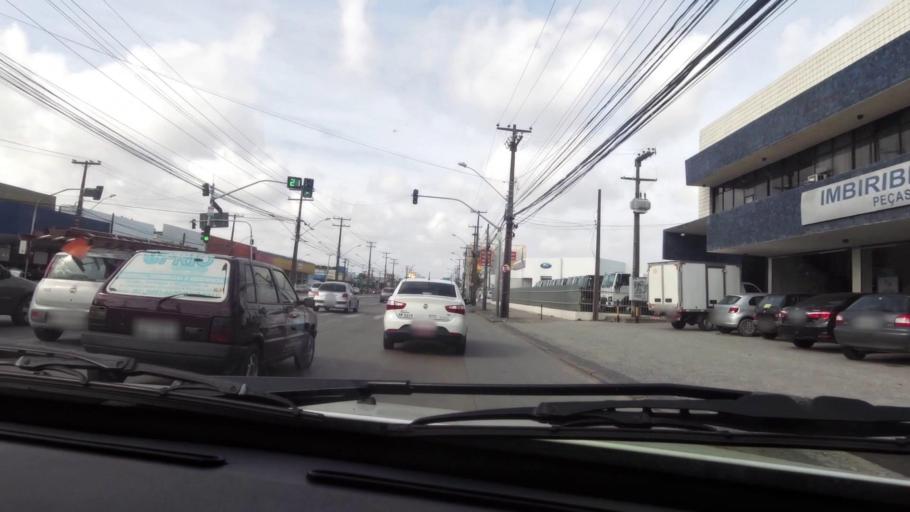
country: BR
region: Pernambuco
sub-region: Recife
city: Recife
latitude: -8.1057
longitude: -34.9116
